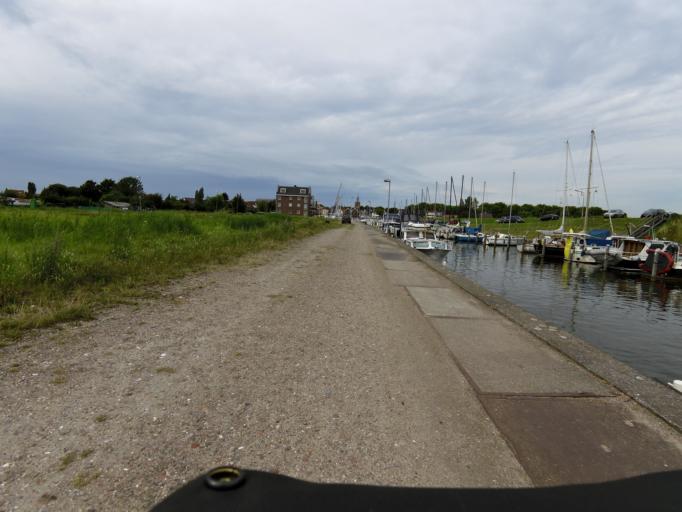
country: NL
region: South Holland
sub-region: Gemeente Goeree-Overflakkee
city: Middelharnis
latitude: 51.6865
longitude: 4.2120
